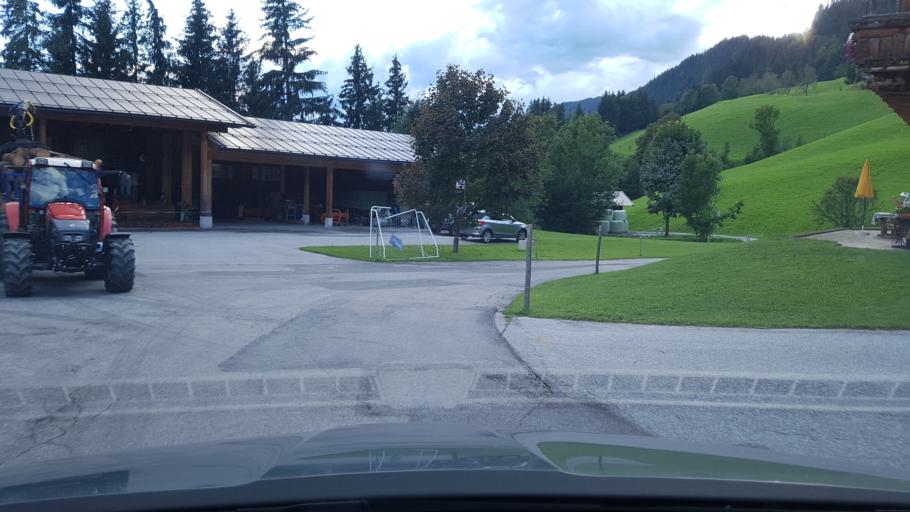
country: AT
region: Salzburg
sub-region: Politischer Bezirk Sankt Johann im Pongau
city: Goldegg
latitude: 47.3406
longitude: 13.1030
